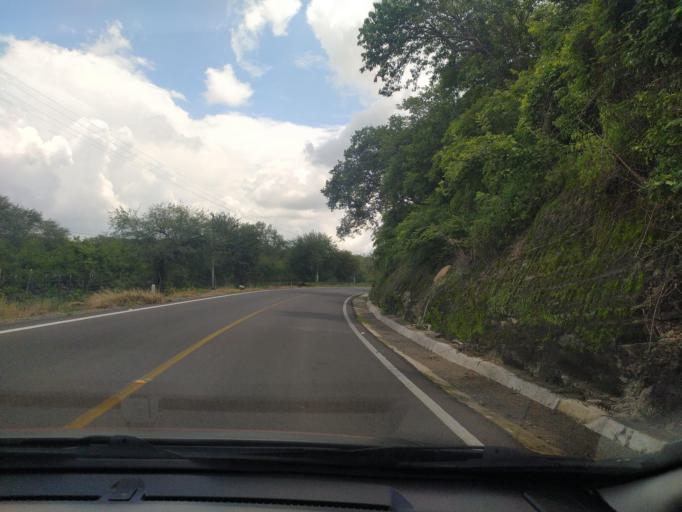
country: MX
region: Jalisco
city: Villa Corona
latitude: 20.3862
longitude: -103.6733
